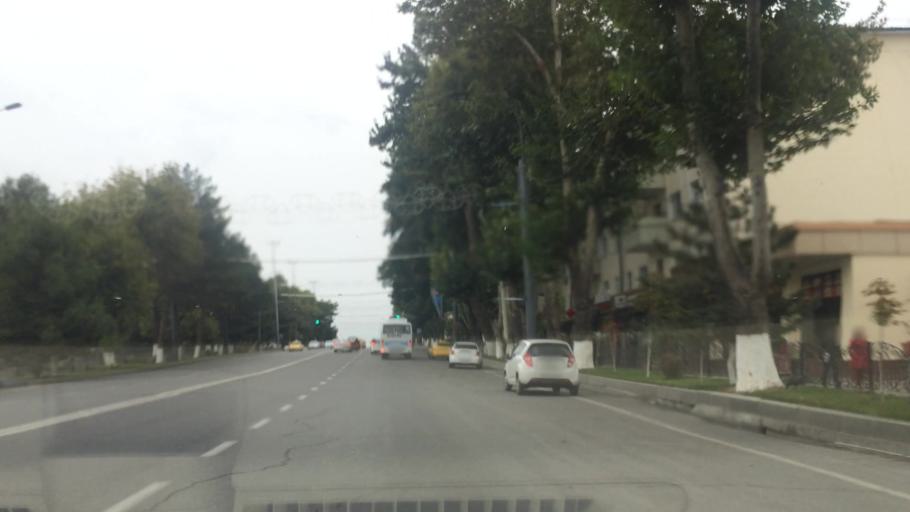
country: UZ
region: Samarqand
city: Samarqand
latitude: 39.6534
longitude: 66.9741
